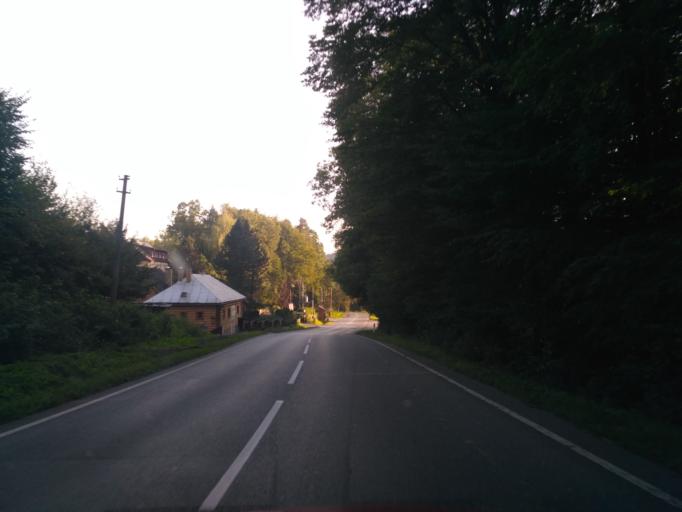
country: SK
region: Presovsky
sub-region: Okres Presov
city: Presov
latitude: 48.9886
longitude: 21.1772
